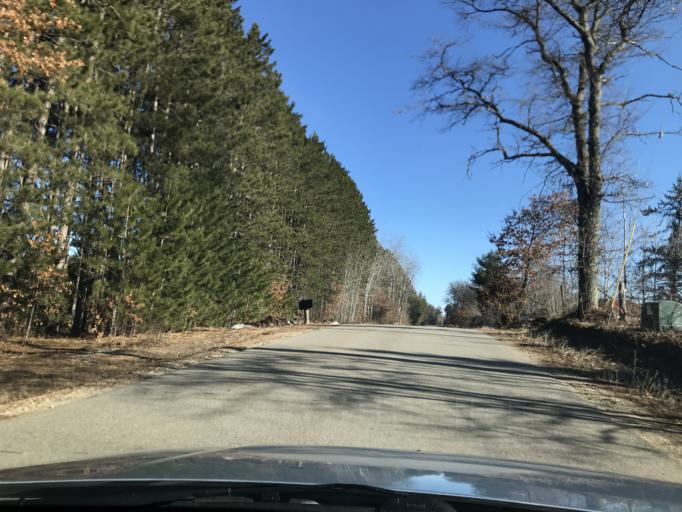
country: US
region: Wisconsin
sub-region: Marinette County
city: Niagara
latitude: 45.3941
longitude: -88.0790
